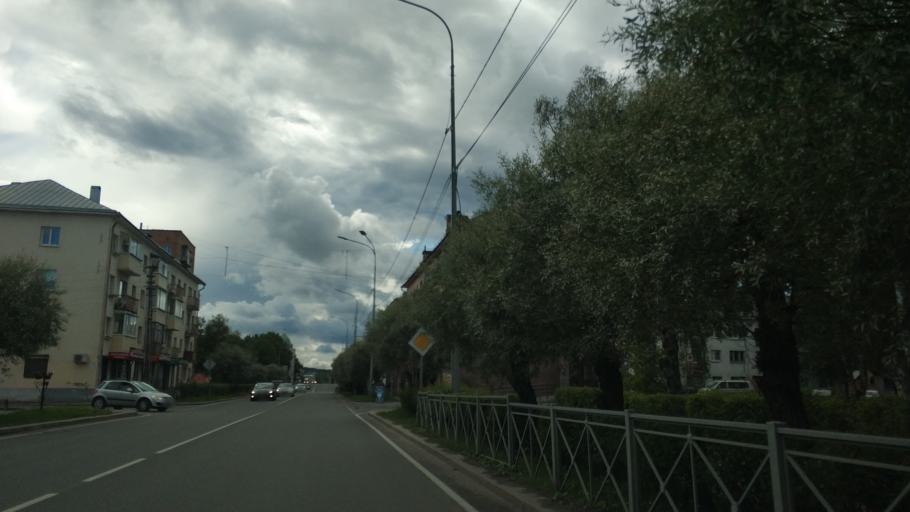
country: RU
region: Republic of Karelia
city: Sortavala
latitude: 61.7045
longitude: 30.6940
